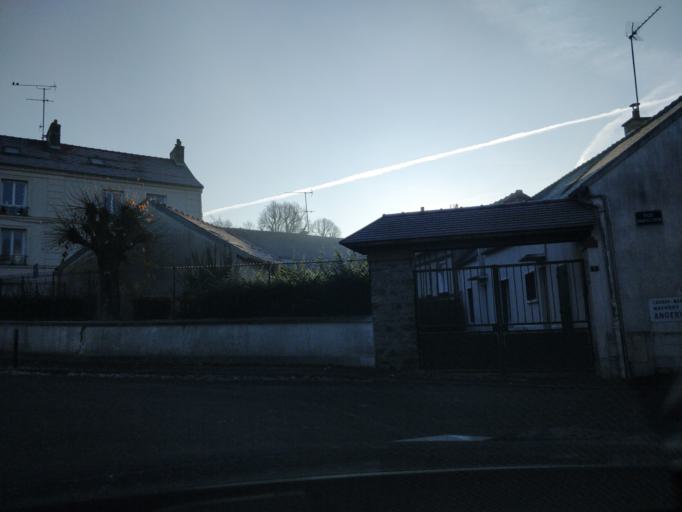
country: FR
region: Ile-de-France
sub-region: Departement de l'Essonne
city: Briis-sous-Forges
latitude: 48.6236
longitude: 2.1217
